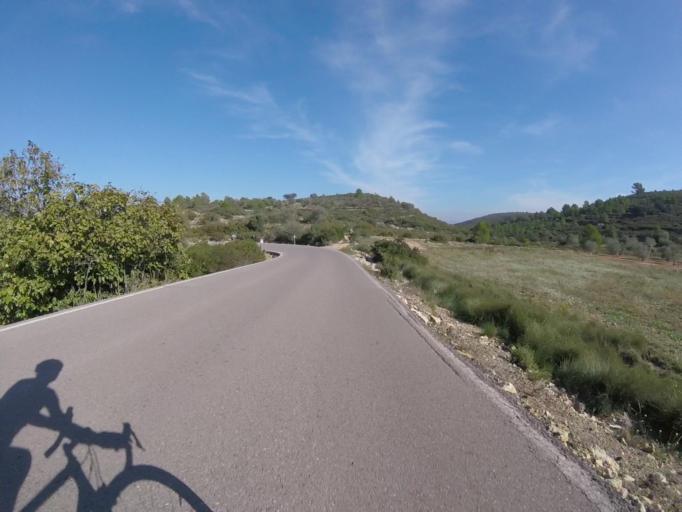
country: ES
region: Valencia
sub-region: Provincia de Castello
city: Benlloch
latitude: 40.2453
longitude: 0.0788
